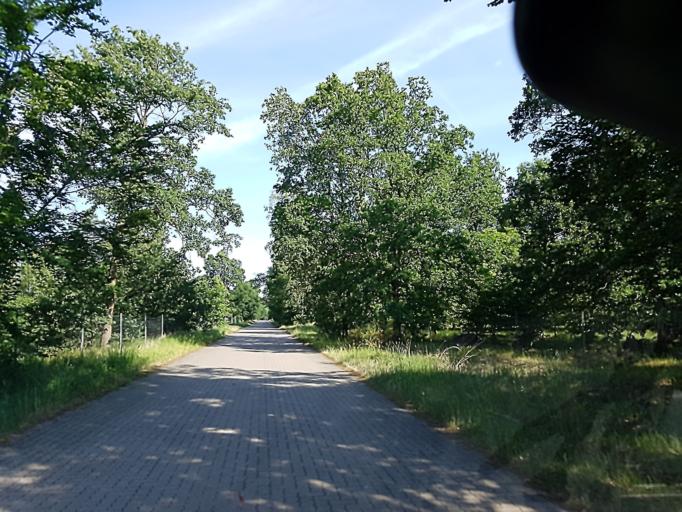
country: DE
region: Brandenburg
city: Gorzke
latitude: 52.0438
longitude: 12.2749
